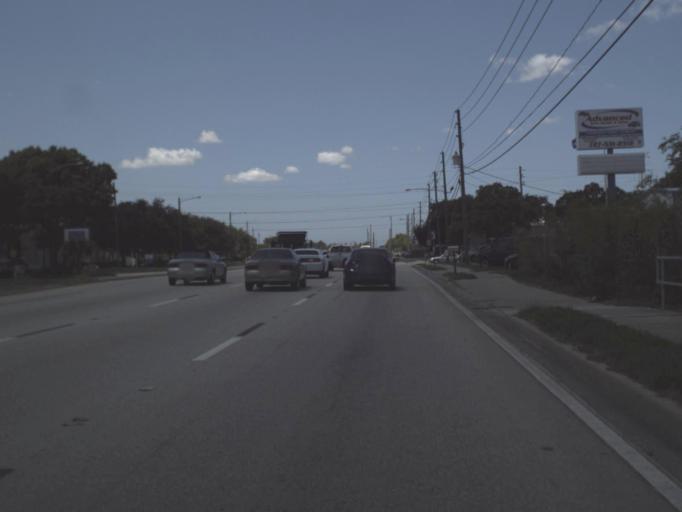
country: US
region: Florida
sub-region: Pinellas County
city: Pinellas Park
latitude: 27.8793
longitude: -82.6950
